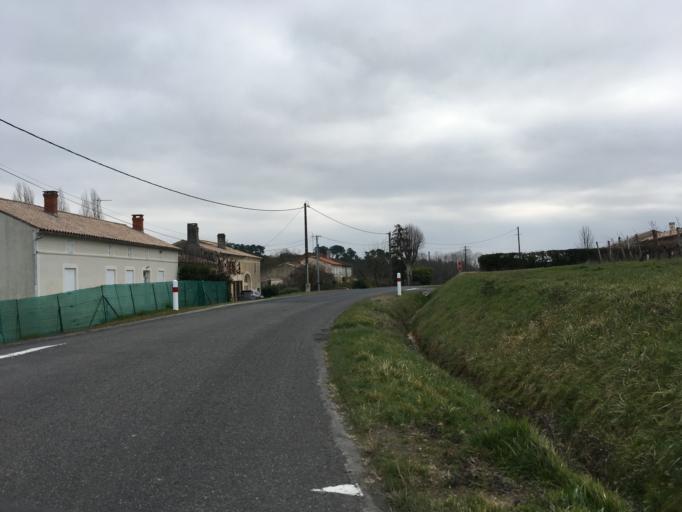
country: FR
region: Poitou-Charentes
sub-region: Departement de la Charente-Maritime
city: Mirambeau
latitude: 45.3303
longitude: -0.5878
